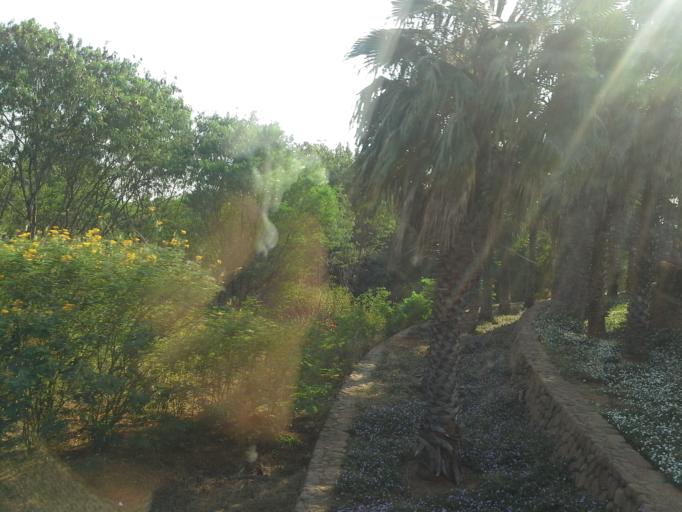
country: IN
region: Telangana
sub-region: Rangareddi
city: Balapur
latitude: 17.2407
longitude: 78.4226
